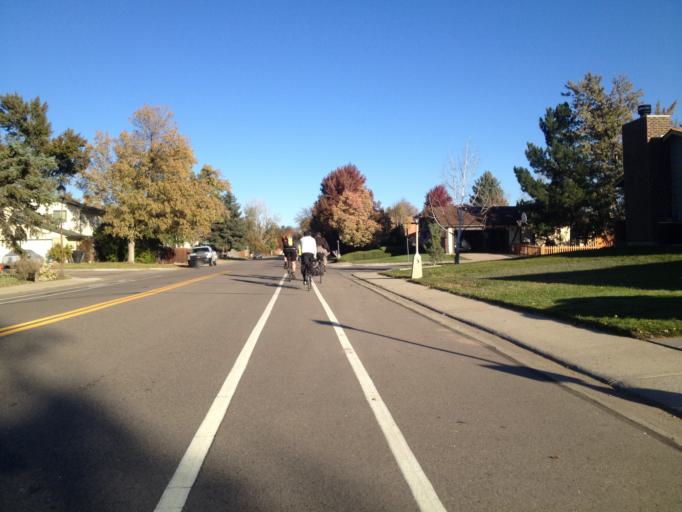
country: US
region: Colorado
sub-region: Boulder County
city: Longmont
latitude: 40.1853
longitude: -105.1359
